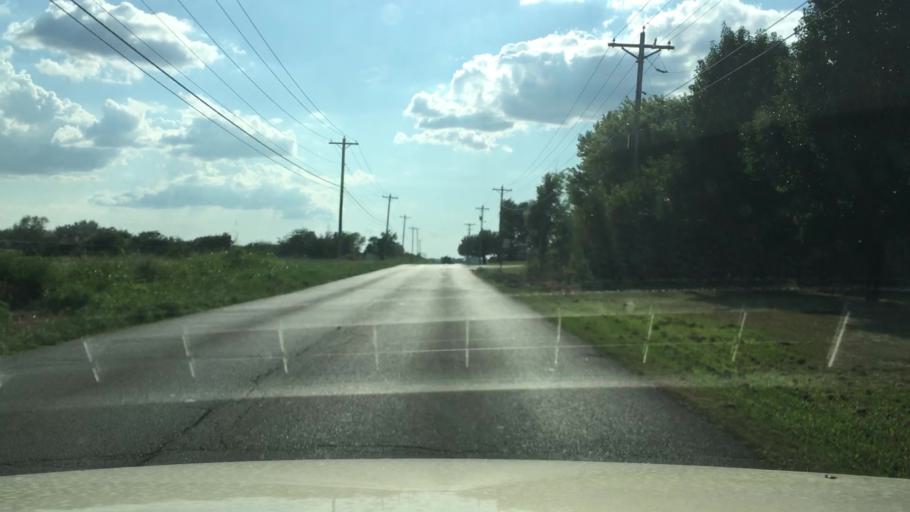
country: US
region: Oklahoma
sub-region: Cherokee County
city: Tahlequah
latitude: 35.9299
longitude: -94.9822
